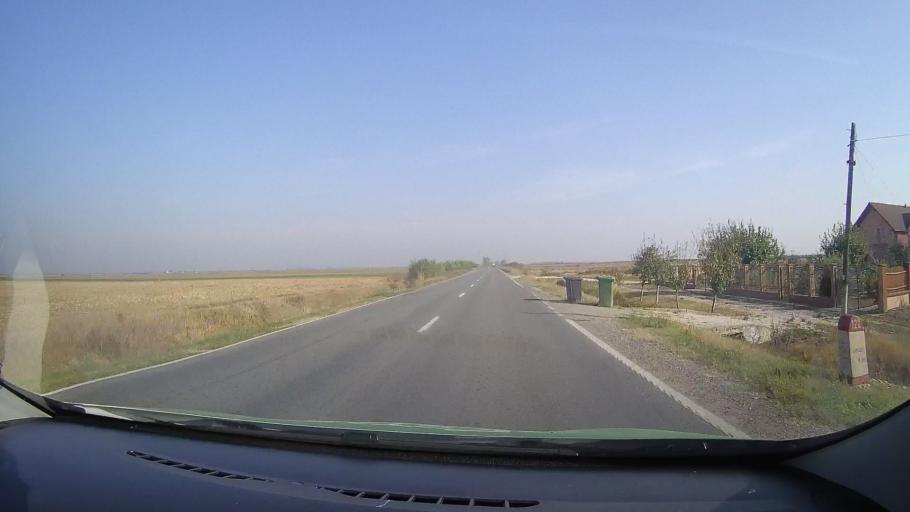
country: RO
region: Arad
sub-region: Comuna Pilu
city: Pilu
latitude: 46.5866
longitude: 21.3449
